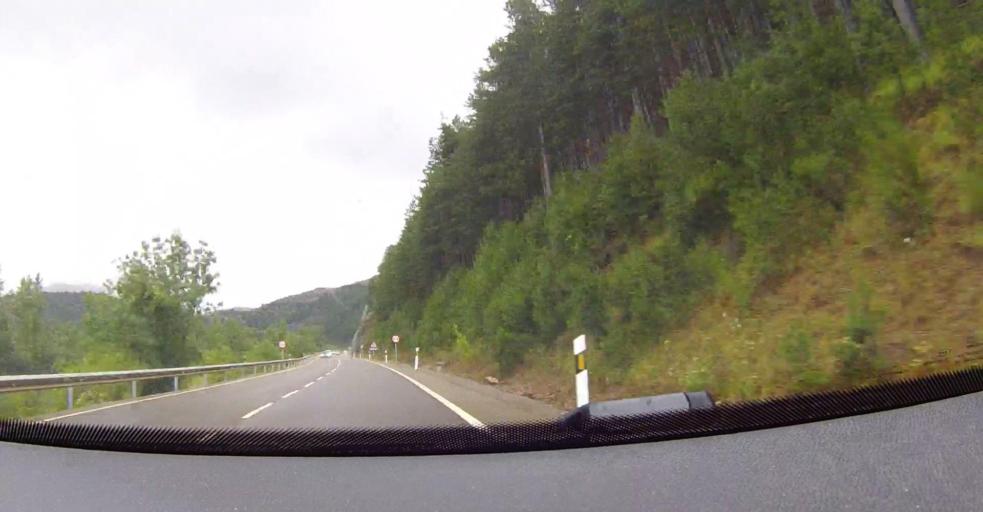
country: ES
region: Castille and Leon
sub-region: Provincia de Leon
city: Cistierna
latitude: 42.8188
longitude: -5.1253
